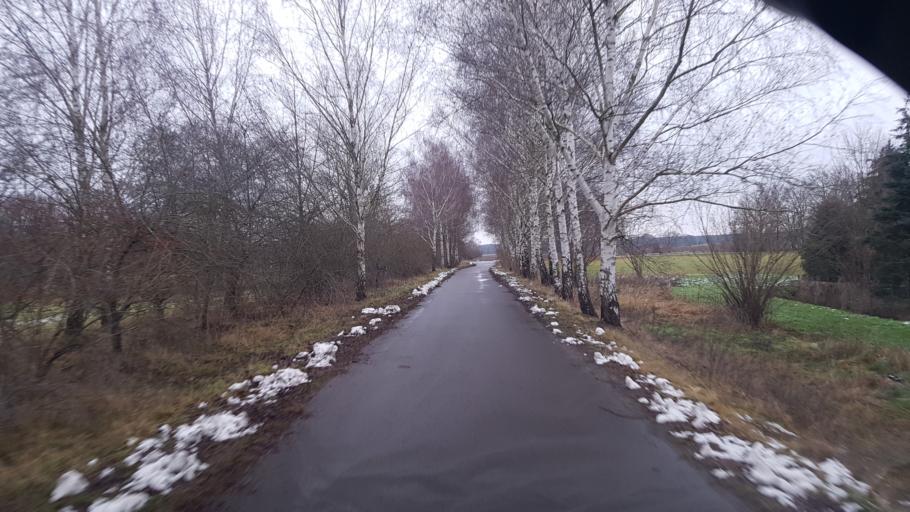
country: DE
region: Brandenburg
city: Lieberose
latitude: 51.9795
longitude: 14.2996
